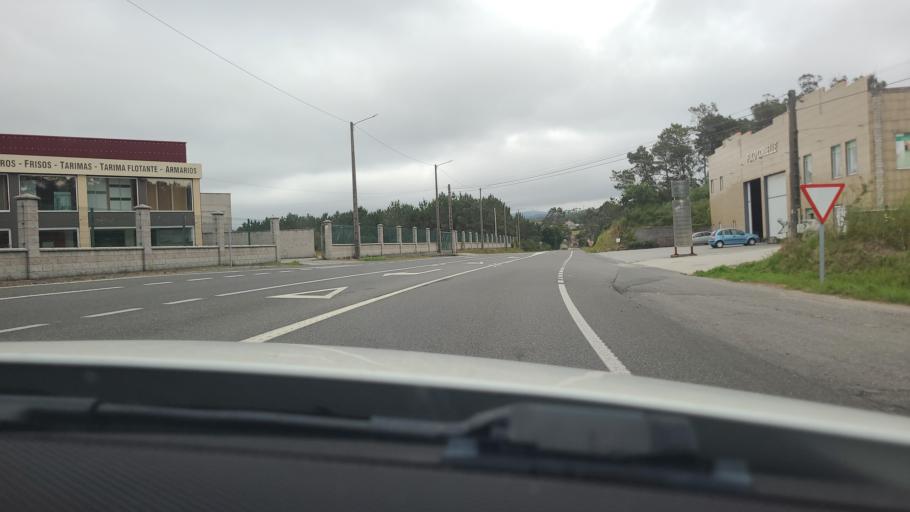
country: ES
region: Galicia
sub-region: Provincia da Coruna
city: Dumbria
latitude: 43.0097
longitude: -9.1667
